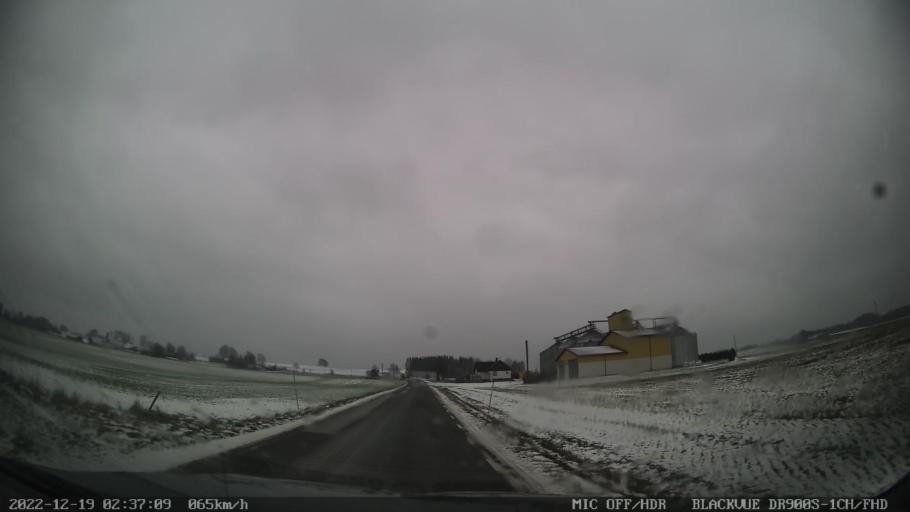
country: SE
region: Skane
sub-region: Tomelilla Kommun
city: Tomelilla
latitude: 55.5204
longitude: 14.0433
